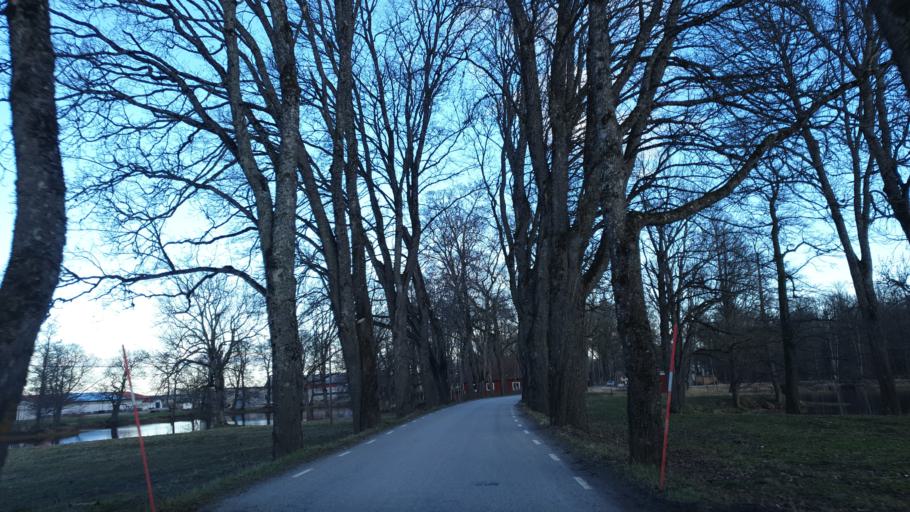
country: SE
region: OErebro
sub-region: Orebro Kommun
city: Garphyttan
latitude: 59.3451
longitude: 15.0063
